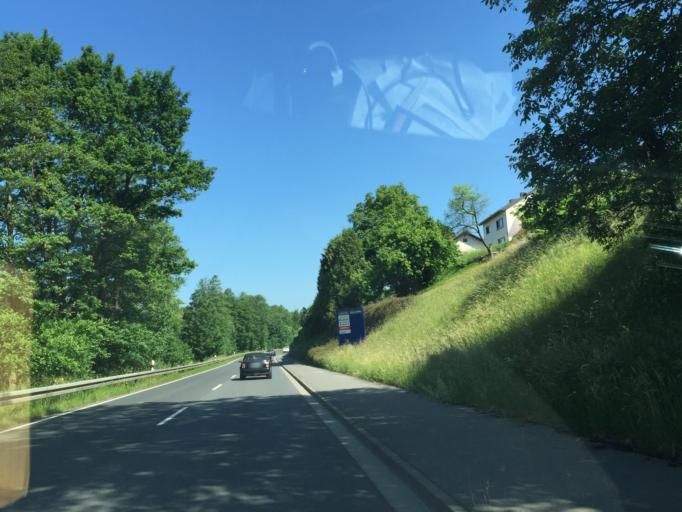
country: DE
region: Hesse
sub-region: Regierungsbezirk Darmstadt
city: Erbach
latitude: 49.6415
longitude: 8.9969
